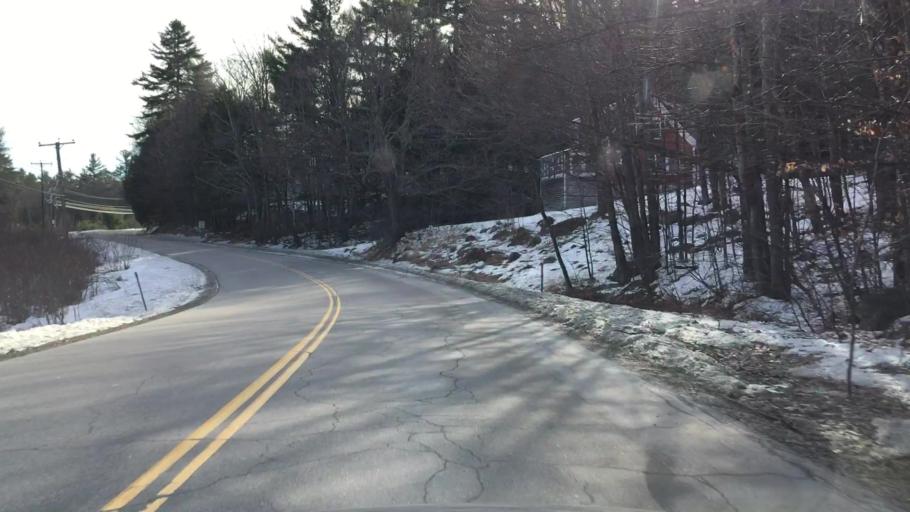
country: US
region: New Hampshire
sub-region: Sullivan County
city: Sunapee
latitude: 43.4390
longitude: -72.0657
